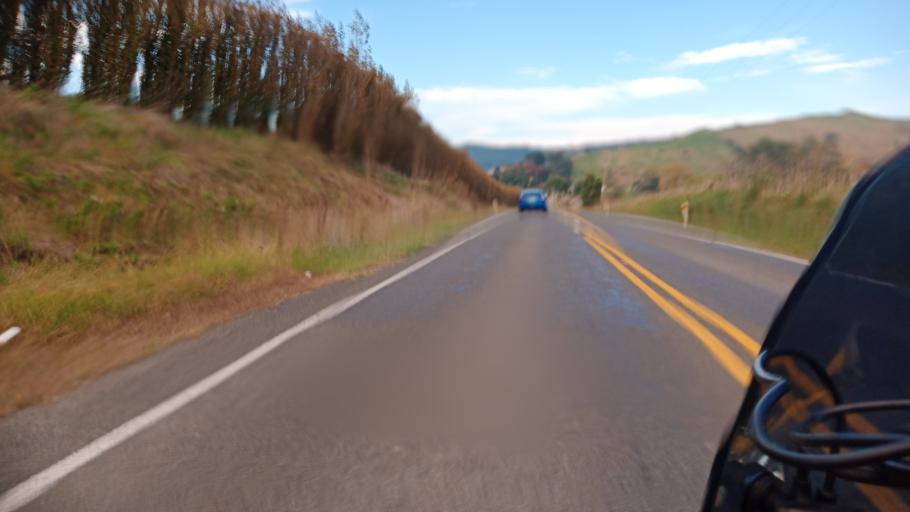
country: NZ
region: Gisborne
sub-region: Gisborne District
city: Gisborne
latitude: -38.7978
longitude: 177.9067
